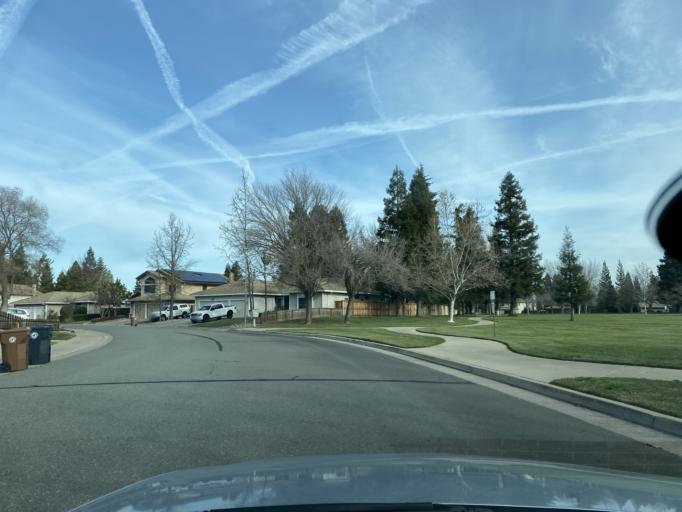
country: US
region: California
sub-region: Sacramento County
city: Elk Grove
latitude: 38.4299
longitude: -121.3789
